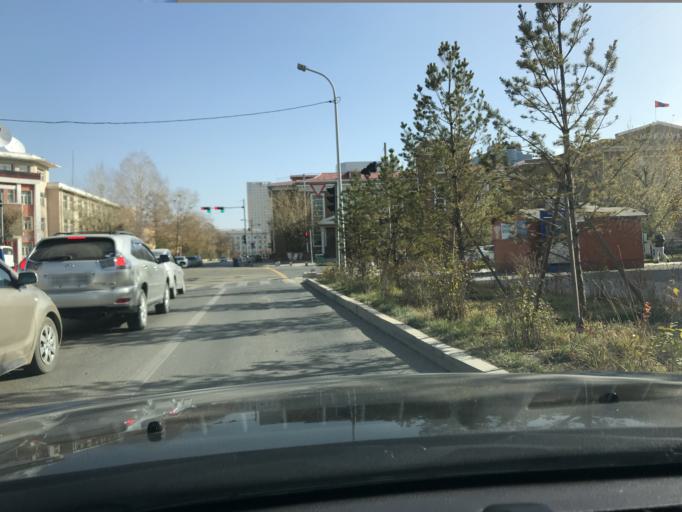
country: MN
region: Ulaanbaatar
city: Ulaanbaatar
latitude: 47.9200
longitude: 106.9107
